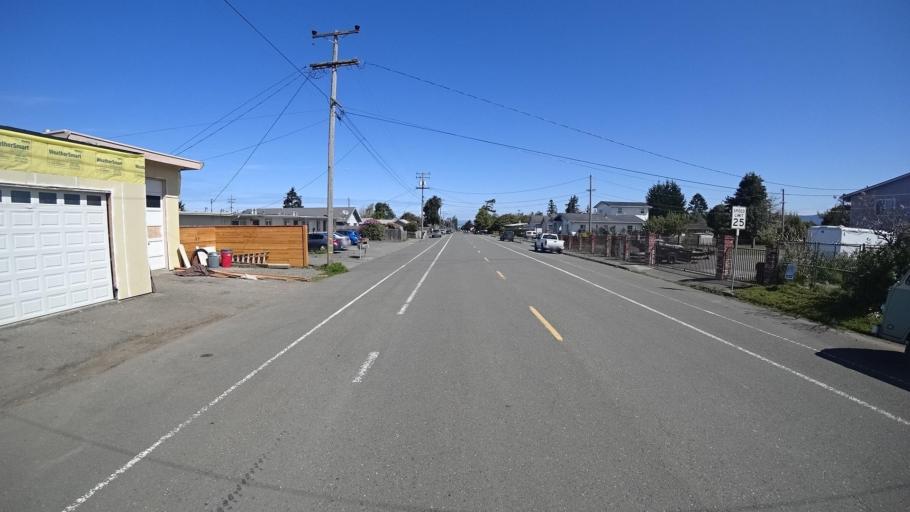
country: US
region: California
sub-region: Humboldt County
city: Myrtletown
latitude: 40.7882
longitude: -124.1262
